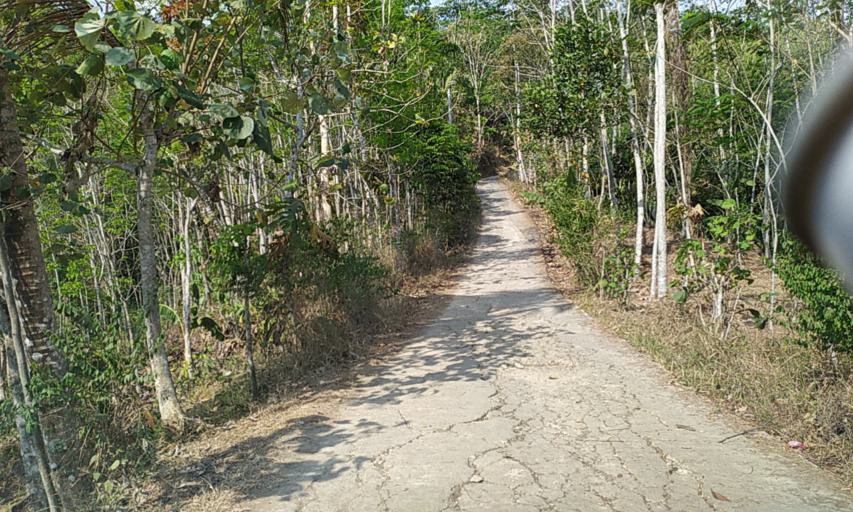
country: ID
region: Central Java
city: Jambuluwuk
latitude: -7.3150
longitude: 108.9073
